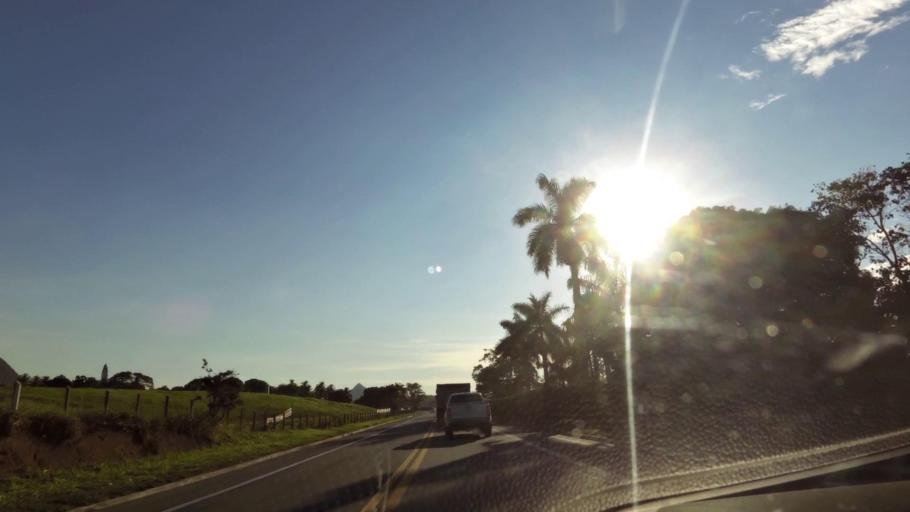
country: BR
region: Espirito Santo
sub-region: Guarapari
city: Guarapari
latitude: -20.6055
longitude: -40.5049
